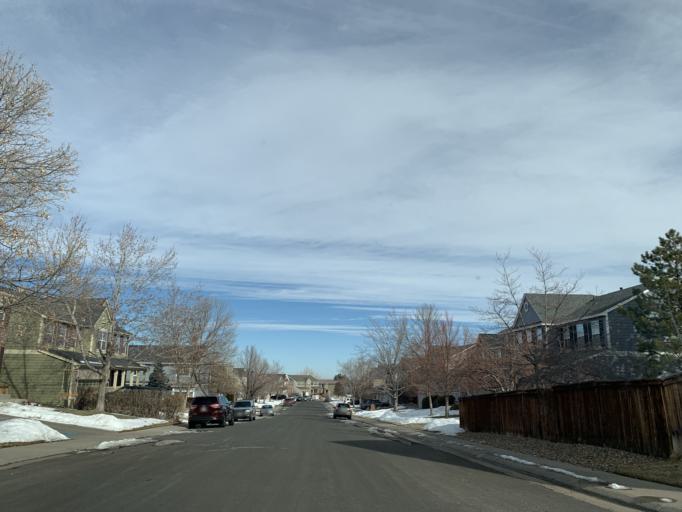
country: US
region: Colorado
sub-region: Douglas County
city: Carriage Club
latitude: 39.5336
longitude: -104.9368
